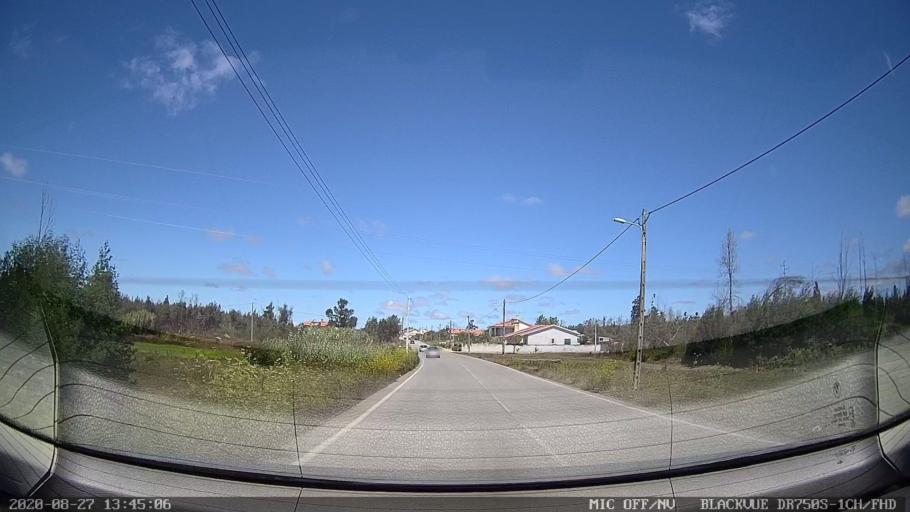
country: PT
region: Coimbra
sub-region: Mira
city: Mira
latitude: 40.4082
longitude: -8.7346
